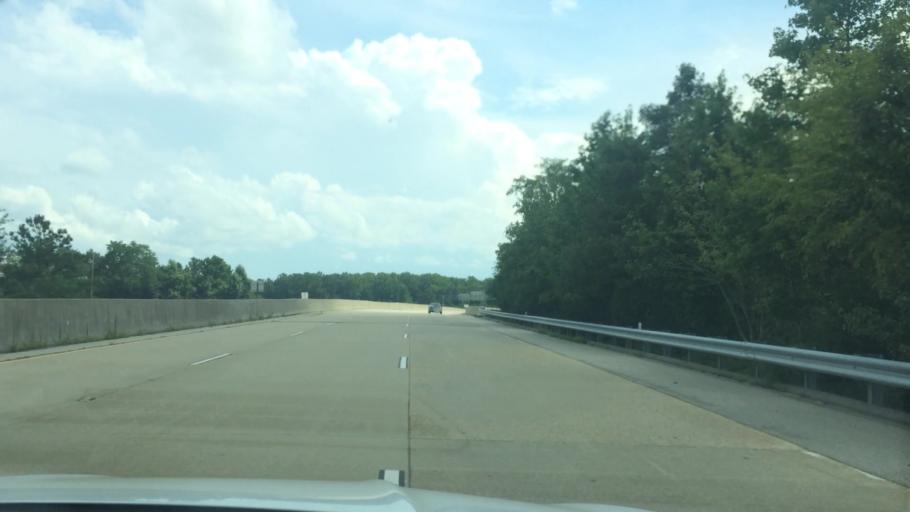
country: US
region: Virginia
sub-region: City of Williamsburg
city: Williamsburg
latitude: 37.2390
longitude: -76.6345
